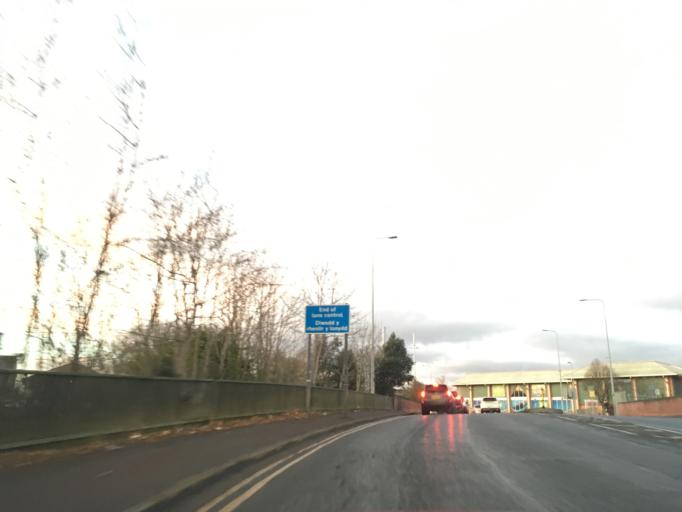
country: GB
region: Wales
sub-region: Cardiff
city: Cardiff
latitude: 51.4952
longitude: -3.1913
